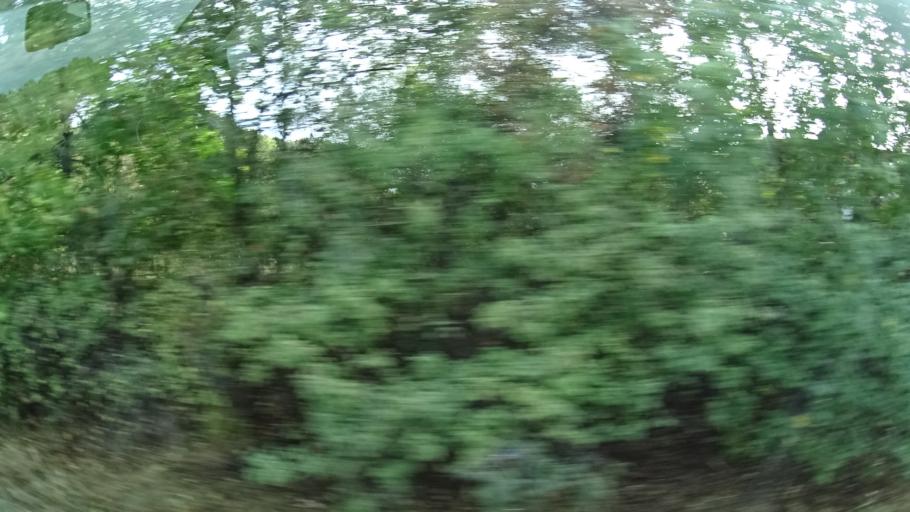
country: DE
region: Hesse
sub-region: Regierungsbezirk Kassel
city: Hilders
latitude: 50.5755
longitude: 10.0158
